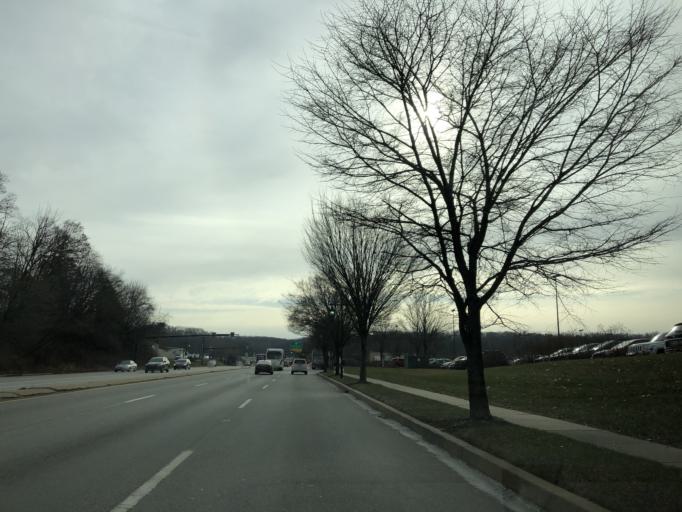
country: US
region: Pennsylvania
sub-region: Chester County
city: Exton
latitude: 40.0247
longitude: -75.6264
